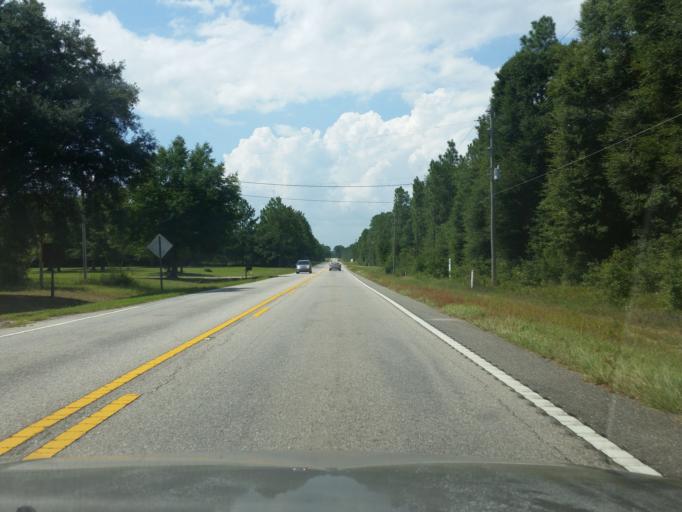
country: US
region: Alabama
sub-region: Baldwin County
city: Elberta
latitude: 30.5162
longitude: -87.4771
